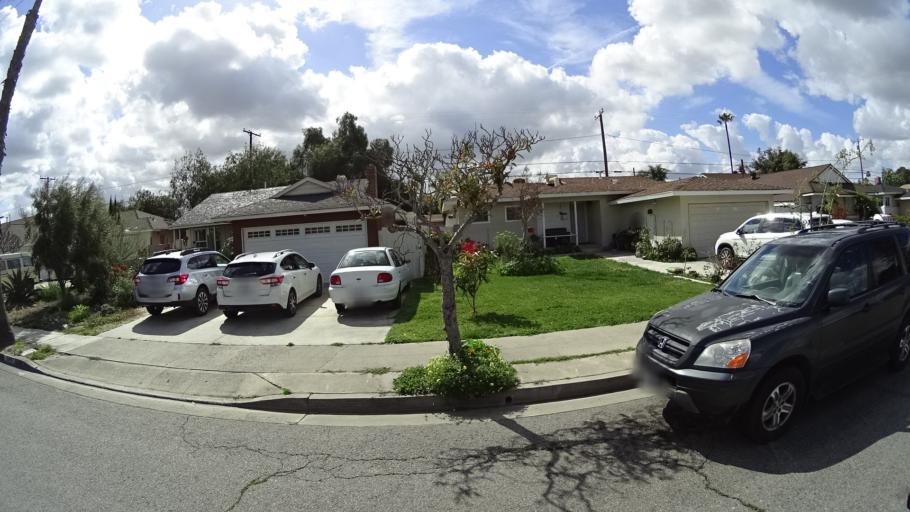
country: US
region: California
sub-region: Orange County
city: Anaheim
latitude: 33.8439
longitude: -117.8918
